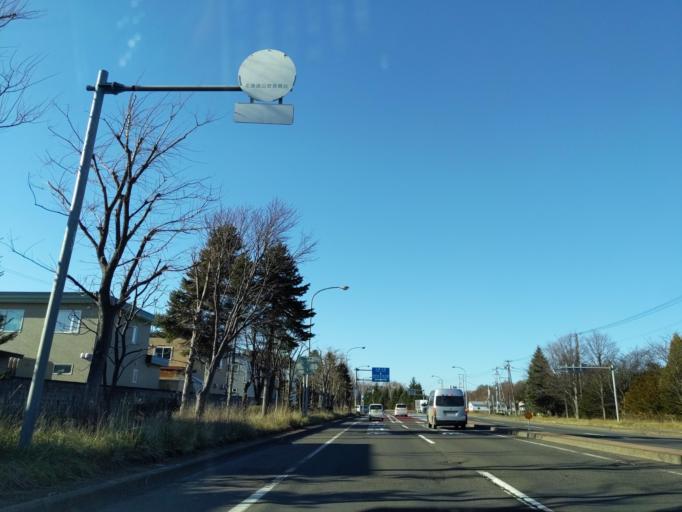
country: JP
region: Hokkaido
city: Kitahiroshima
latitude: 42.9051
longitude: 141.5620
